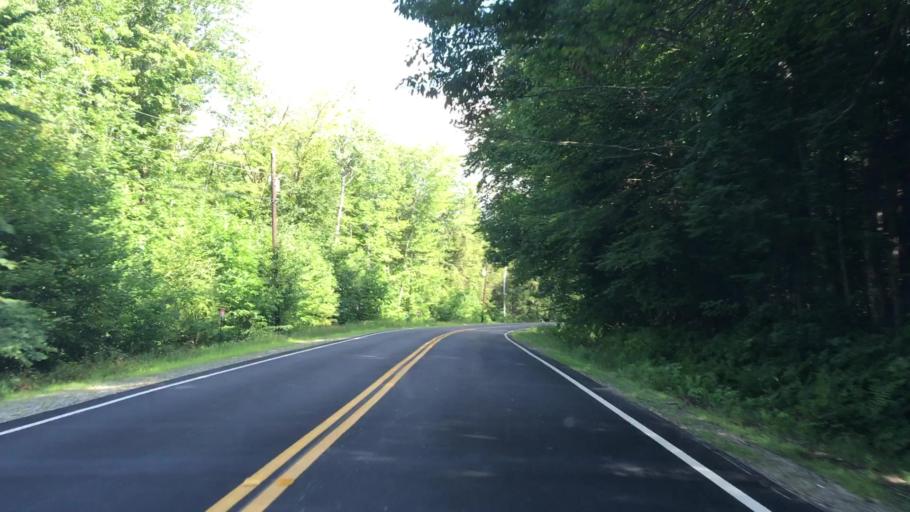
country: US
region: New Hampshire
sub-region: Grafton County
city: North Haverhill
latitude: 44.1186
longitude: -71.9165
